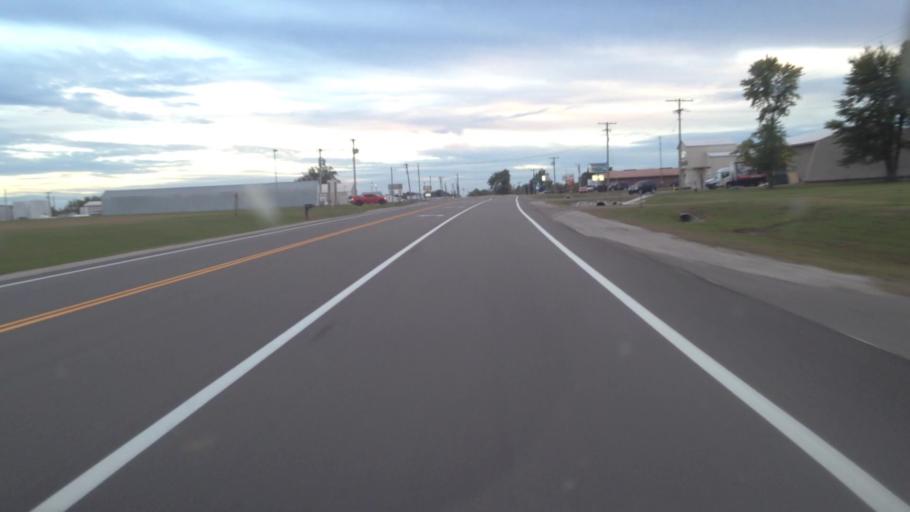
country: US
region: Kansas
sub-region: Anderson County
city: Garnett
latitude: 38.2943
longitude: -95.2491
